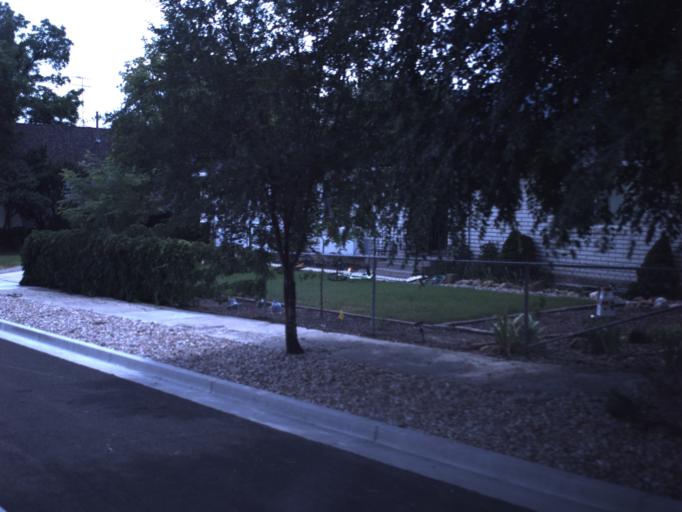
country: US
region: Utah
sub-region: Sanpete County
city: Fountain Green
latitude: 39.6306
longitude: -111.6345
